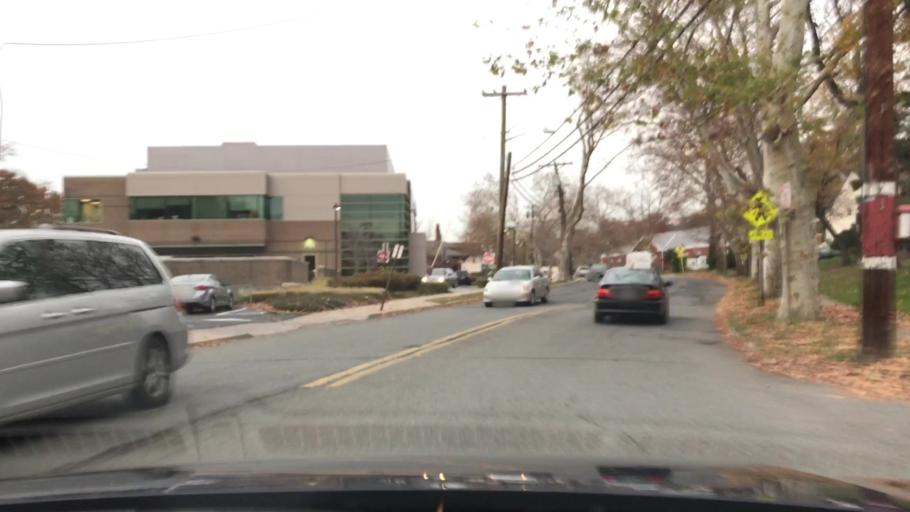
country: US
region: New Jersey
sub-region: Bergen County
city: Teaneck
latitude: 40.8859
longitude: -74.0207
